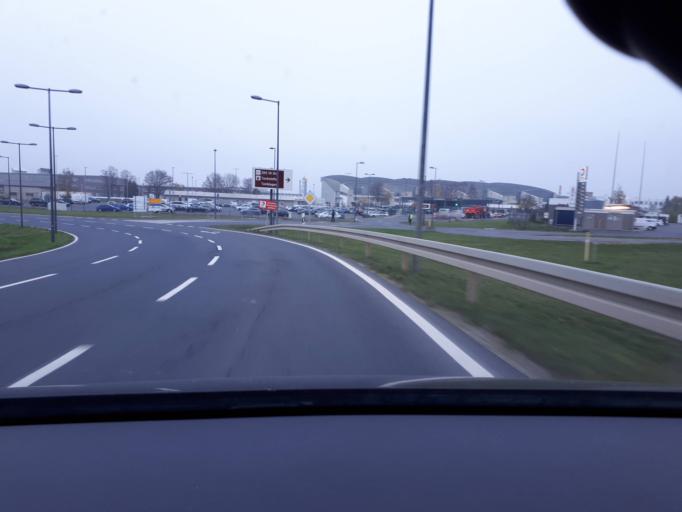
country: DE
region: Brandenburg
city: Schonefeld
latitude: 52.3693
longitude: 13.5269
